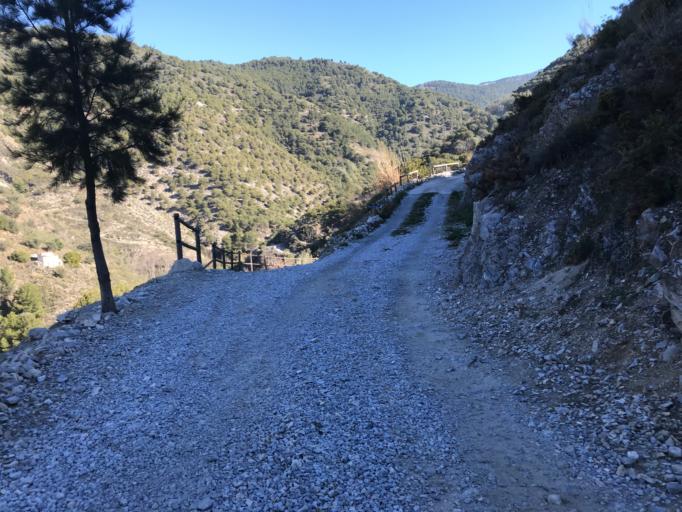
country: ES
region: Andalusia
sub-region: Provincia de Malaga
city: Canillas de Albaida
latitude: 36.8481
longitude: -3.9873
